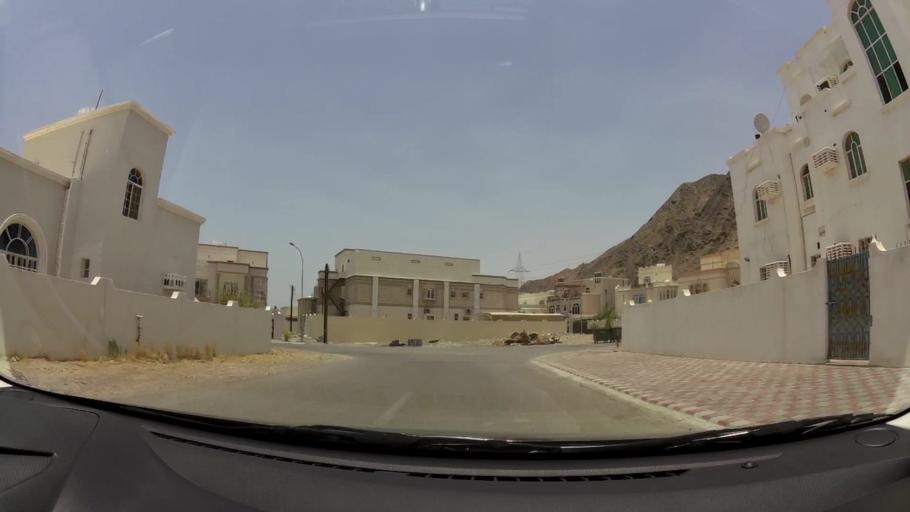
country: OM
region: Muhafazat Masqat
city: Bawshar
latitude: 23.5695
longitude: 58.4282
